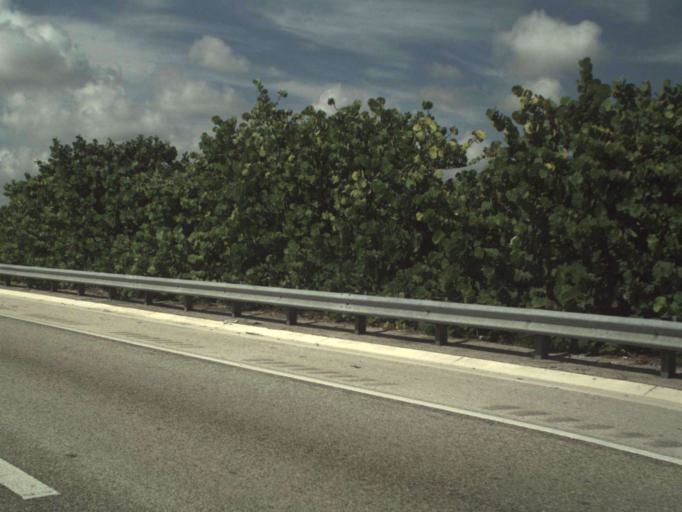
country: US
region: Florida
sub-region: Palm Beach County
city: Lake Clarke Shores
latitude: 26.6631
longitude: -80.0712
